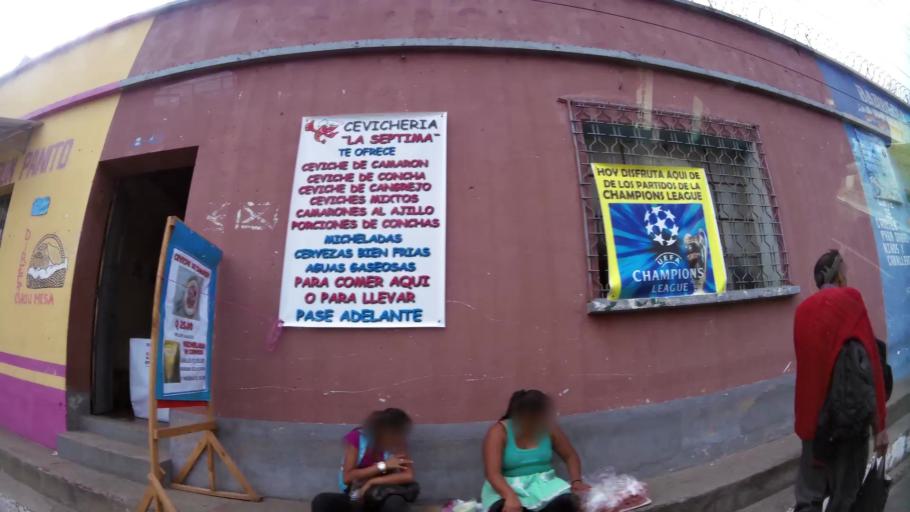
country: GT
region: Guatemala
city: Mixco
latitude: 14.6287
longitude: -90.6075
